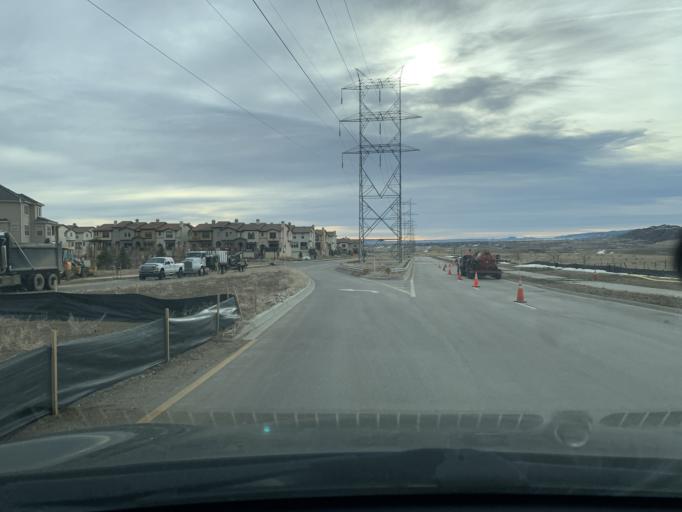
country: US
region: Colorado
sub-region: Jefferson County
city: West Pleasant View
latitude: 39.6715
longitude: -105.1811
